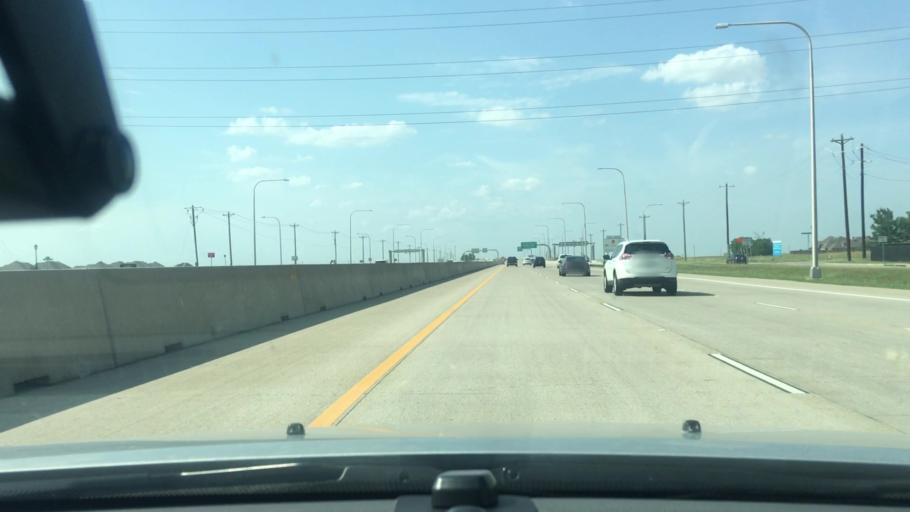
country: US
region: Texas
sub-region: Collin County
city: Frisco
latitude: 33.1817
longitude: -96.8393
